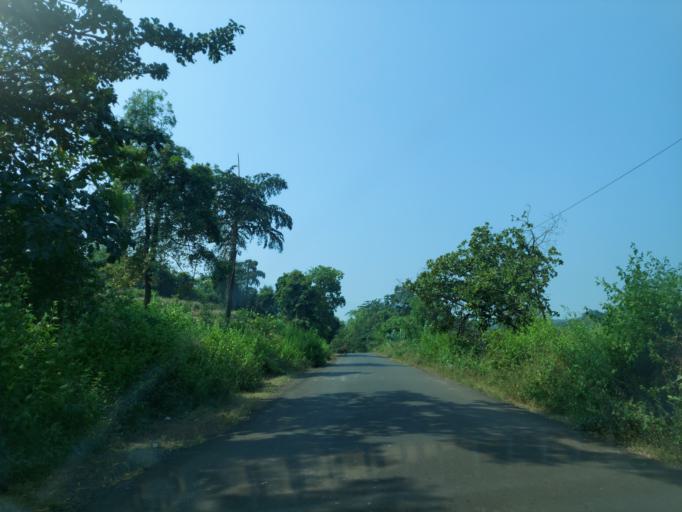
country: IN
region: Maharashtra
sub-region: Sindhudurg
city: Kudal
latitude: 15.9769
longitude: 73.6135
